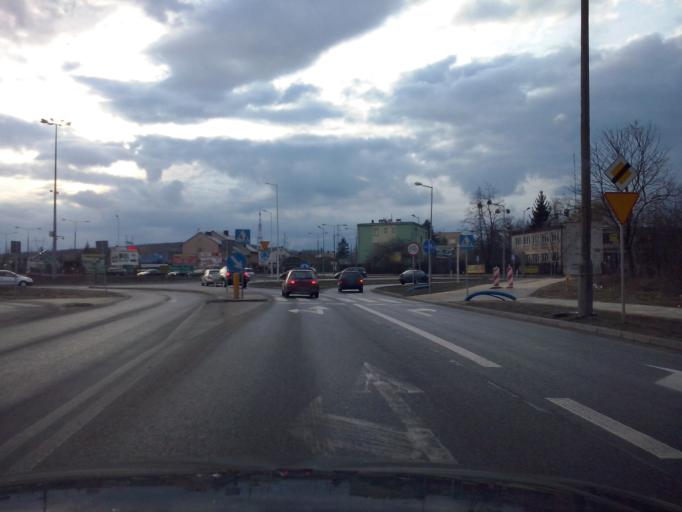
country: PL
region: Lublin Voivodeship
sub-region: Chelm
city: Chelm
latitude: 51.1465
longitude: 23.4379
